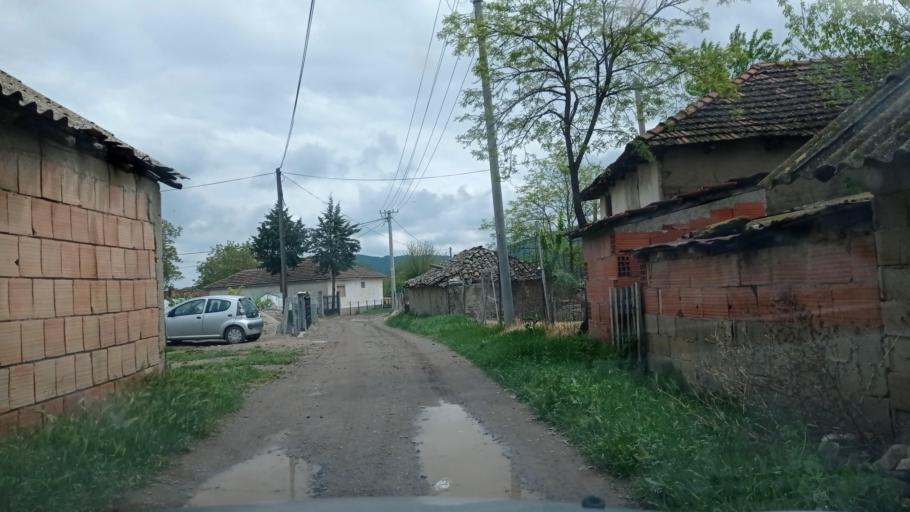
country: MK
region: Lozovo
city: Lozovo
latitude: 41.7660
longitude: 21.8949
